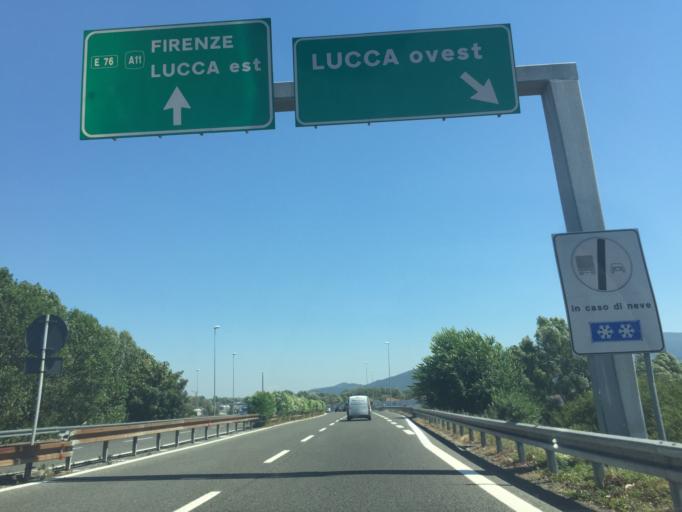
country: IT
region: Tuscany
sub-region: Provincia di Lucca
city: Lucca
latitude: 43.8386
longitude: 10.4635
